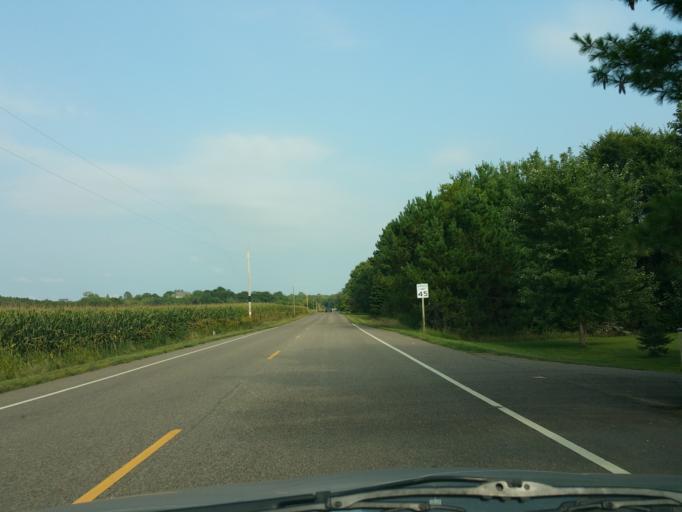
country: US
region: Minnesota
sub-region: Washington County
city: Lake Saint Croix Beach
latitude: 44.9311
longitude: -92.6795
